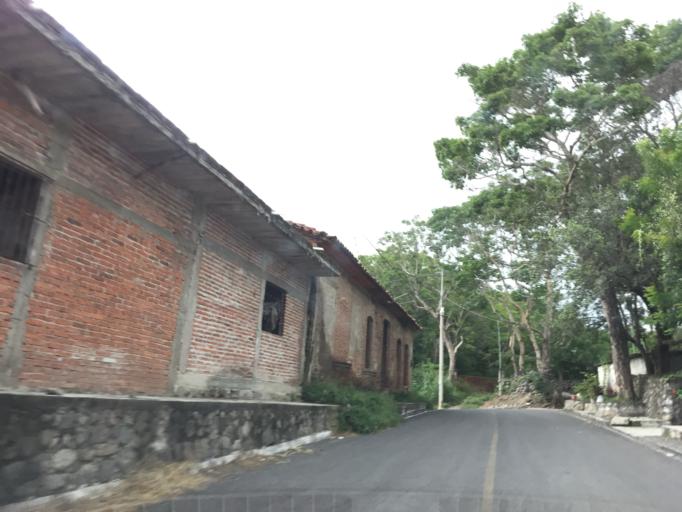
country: MX
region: Colima
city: Comala
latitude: 19.3382
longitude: -103.7764
